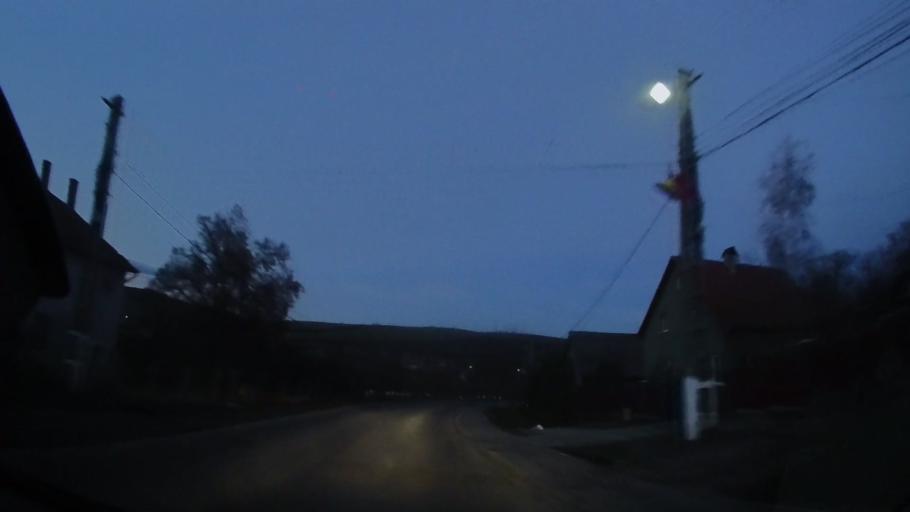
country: RO
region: Mures
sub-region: Comuna Sarmasu
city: Sarmasu
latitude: 46.7571
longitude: 24.1645
